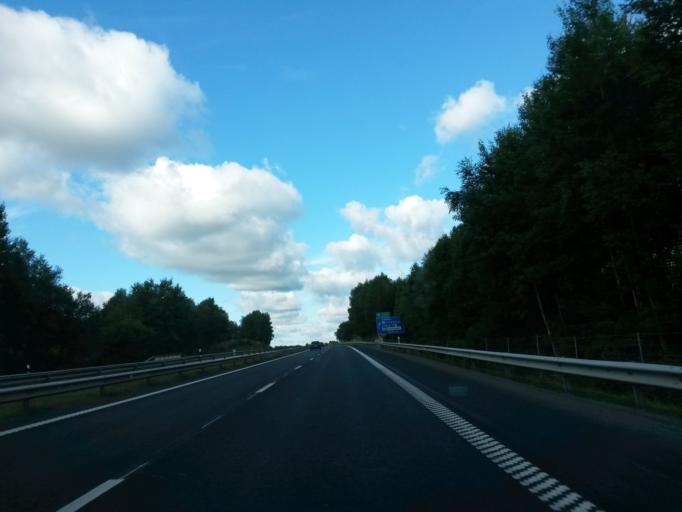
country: SE
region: Vaestra Goetaland
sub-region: Lerums Kommun
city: Stenkullen
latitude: 57.7796
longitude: 12.3074
